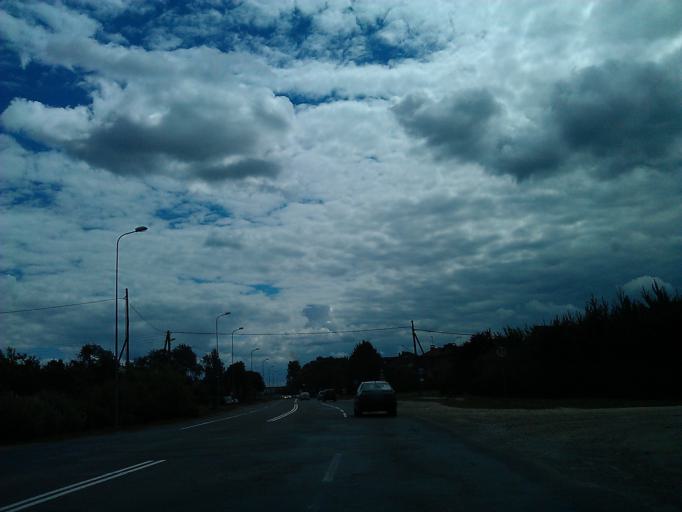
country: LV
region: Jelgava
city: Jelgava
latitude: 56.6451
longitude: 23.6930
